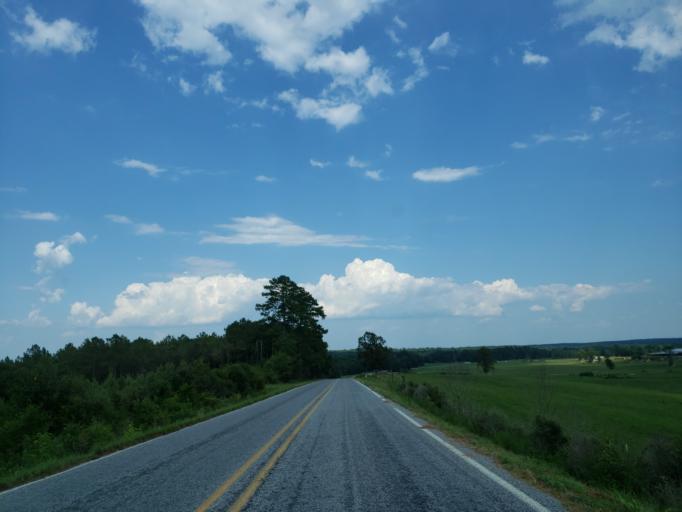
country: US
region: Mississippi
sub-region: Jones County
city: Ellisville
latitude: 31.6235
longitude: -89.3681
